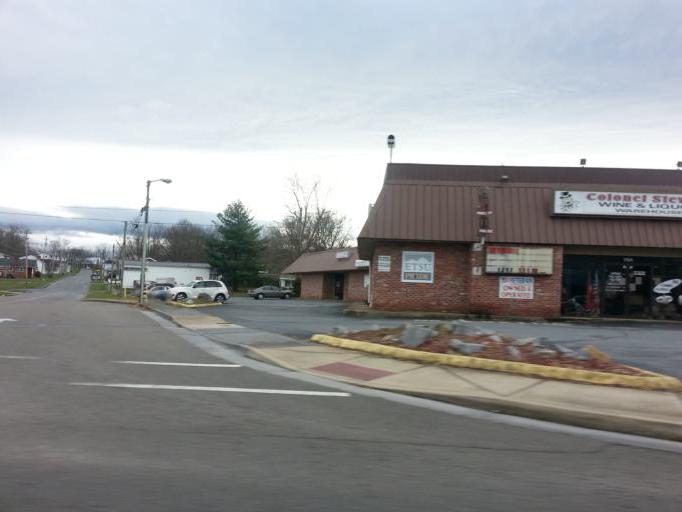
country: US
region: Tennessee
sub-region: Washington County
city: Johnson City
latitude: 36.3163
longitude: -82.3683
